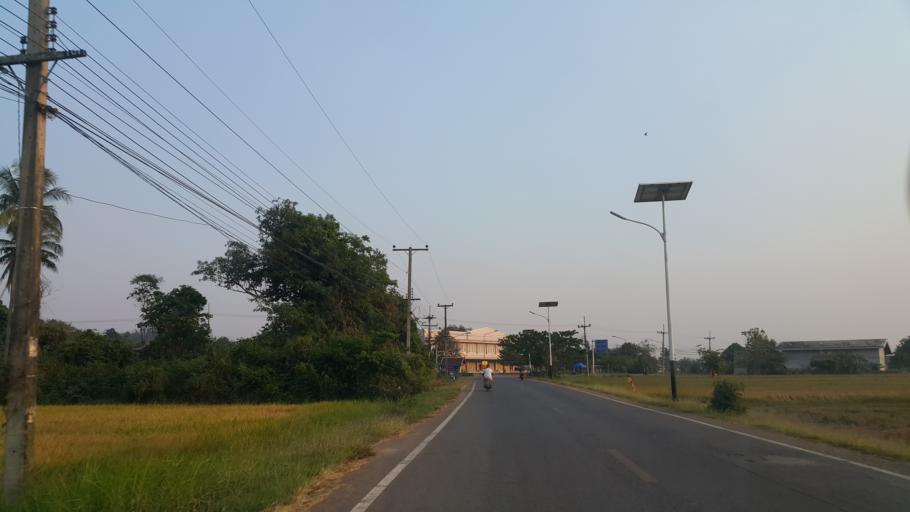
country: TH
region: Sukhothai
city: Thung Saliam
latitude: 17.3355
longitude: 99.5829
